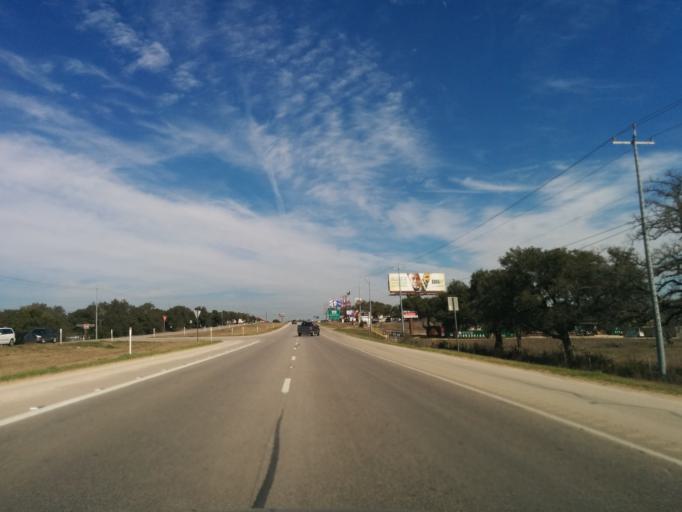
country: US
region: Texas
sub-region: Comal County
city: Bulverde
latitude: 29.7326
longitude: -98.4397
